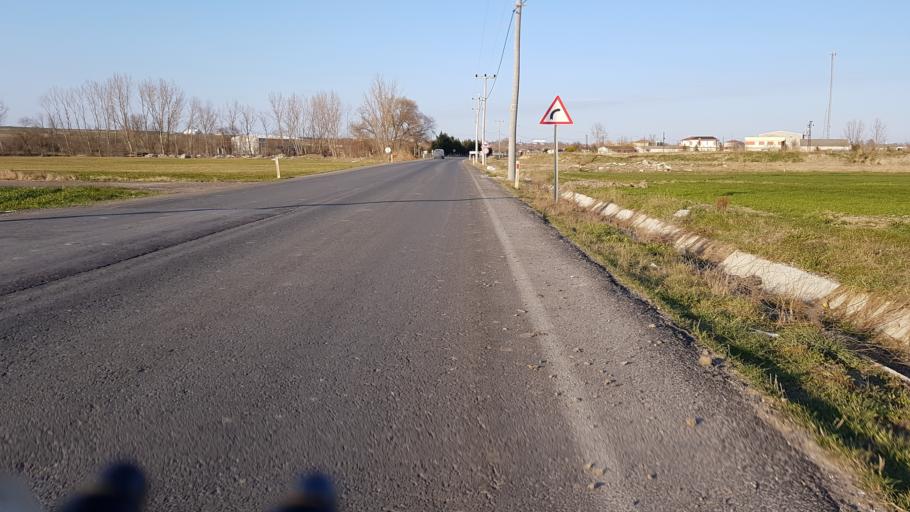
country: TR
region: Tekirdag
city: Beyazkoy
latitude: 41.2976
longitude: 27.7767
